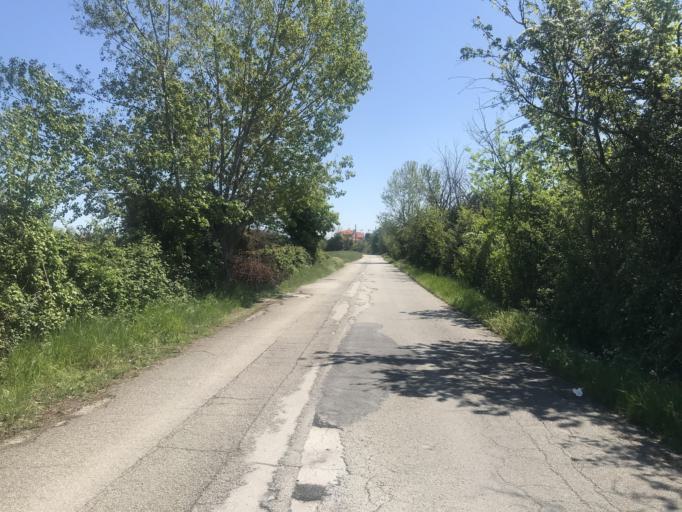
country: IT
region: Emilia-Romagna
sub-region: Provincia di Rimini
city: Rimini
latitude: 44.0721
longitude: 12.5531
